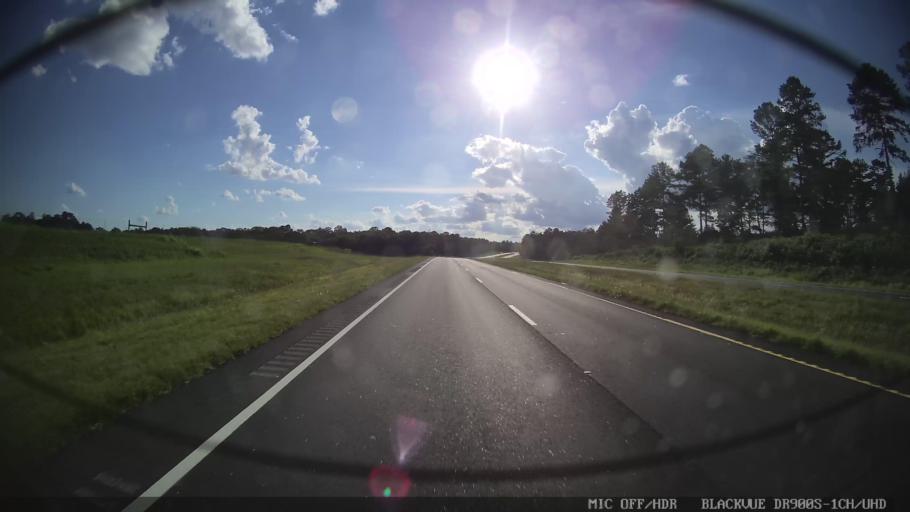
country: US
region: Georgia
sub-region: Floyd County
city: Lindale
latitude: 34.2074
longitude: -85.0828
